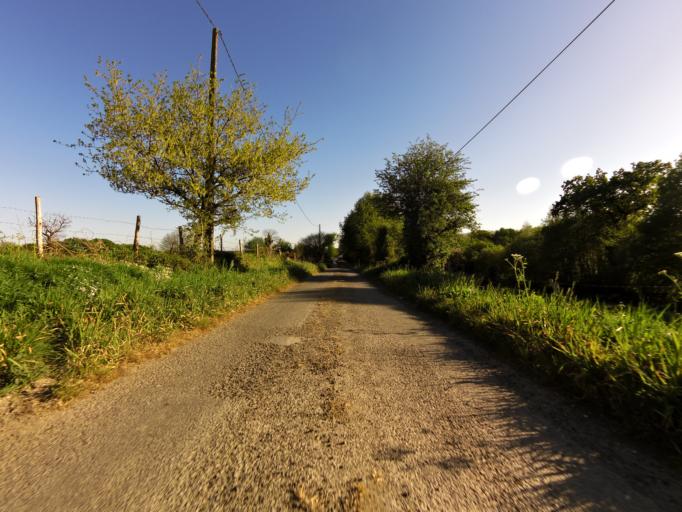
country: FR
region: Brittany
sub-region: Departement du Morbihan
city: Pluherlin
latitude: 47.7221
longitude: -2.3566
